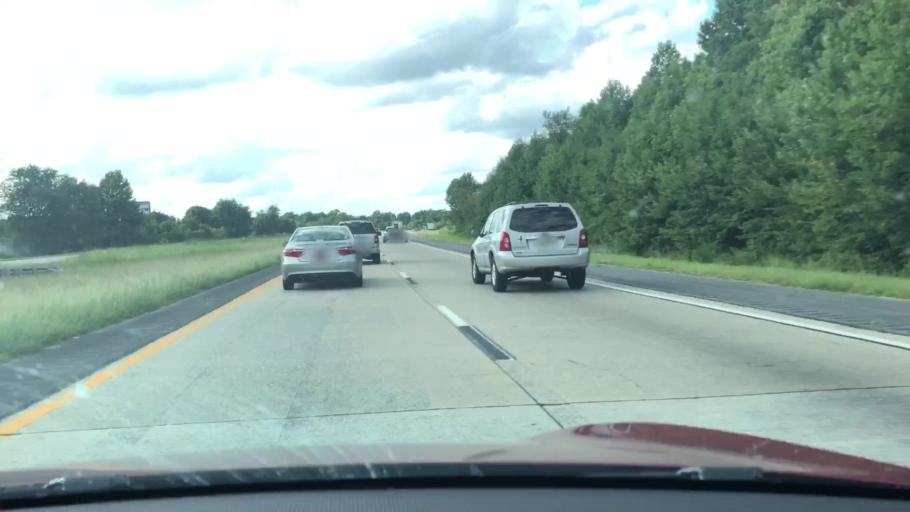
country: US
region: Delaware
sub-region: Kent County
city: Cheswold
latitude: 39.2335
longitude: -75.5864
